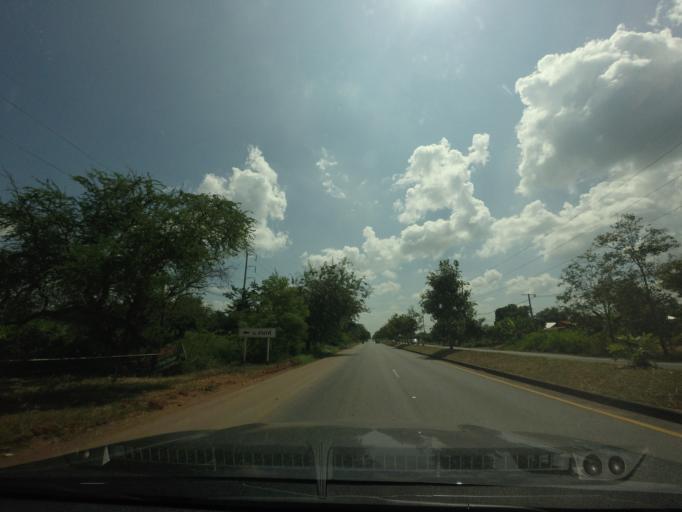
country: TH
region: Phetchabun
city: Nong Phai
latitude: 16.0342
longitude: 101.0774
